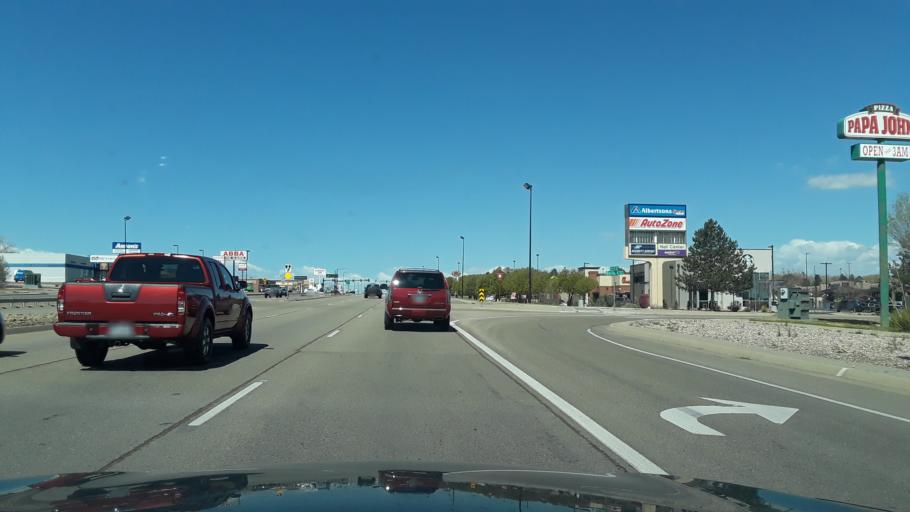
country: US
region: Colorado
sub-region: Pueblo County
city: Pueblo
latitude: 38.3091
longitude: -104.6263
